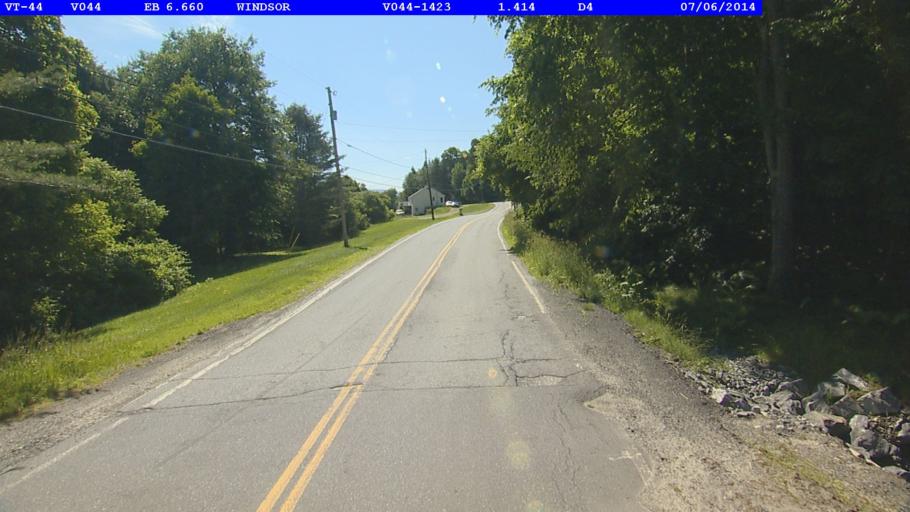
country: US
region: Vermont
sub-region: Windsor County
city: Windsor
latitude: 43.4610
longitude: -72.4272
